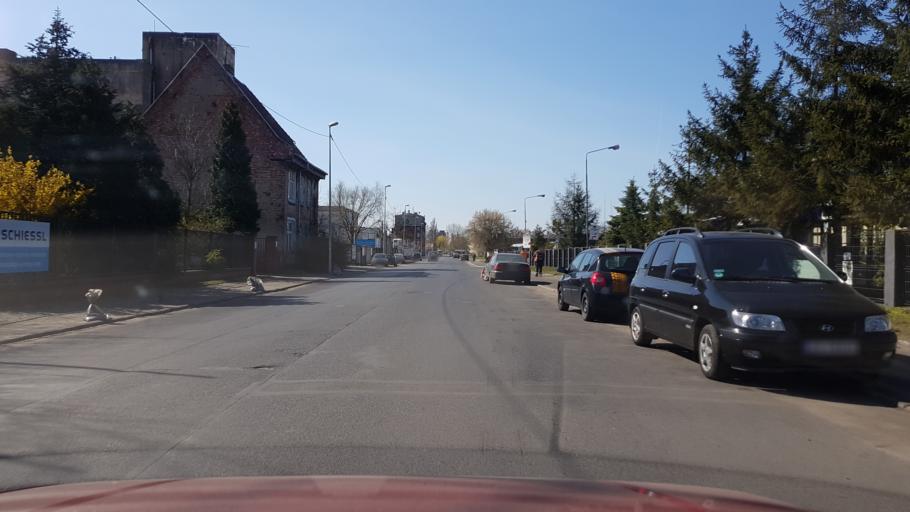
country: PL
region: West Pomeranian Voivodeship
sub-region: Szczecin
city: Szczecin
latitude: 53.4174
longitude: 14.5573
